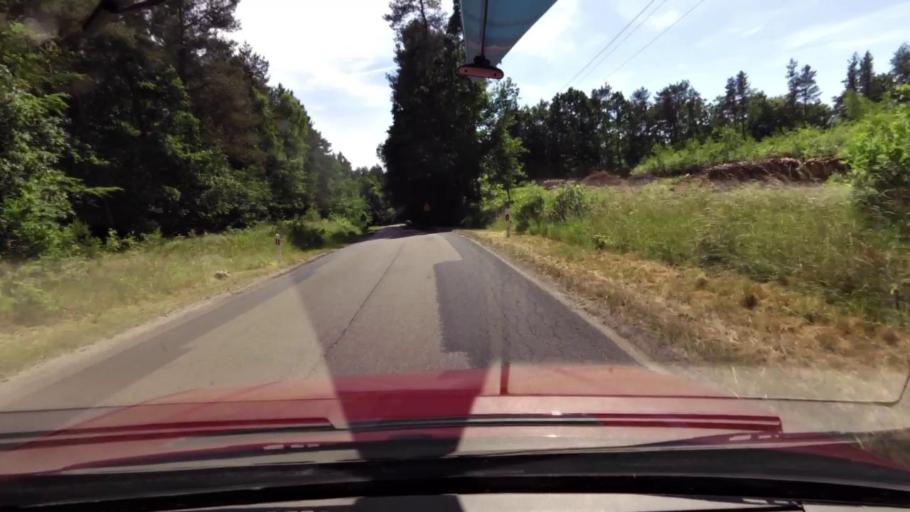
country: PL
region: Pomeranian Voivodeship
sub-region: Powiat slupski
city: Kepice
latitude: 54.2413
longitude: 16.8976
